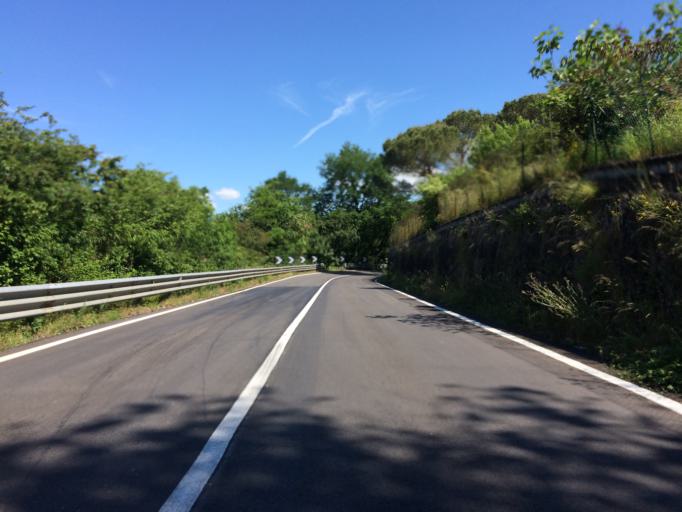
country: IT
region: Tuscany
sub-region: Provincia di Massa-Carrara
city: Terrarossa
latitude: 44.2425
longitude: 9.9593
